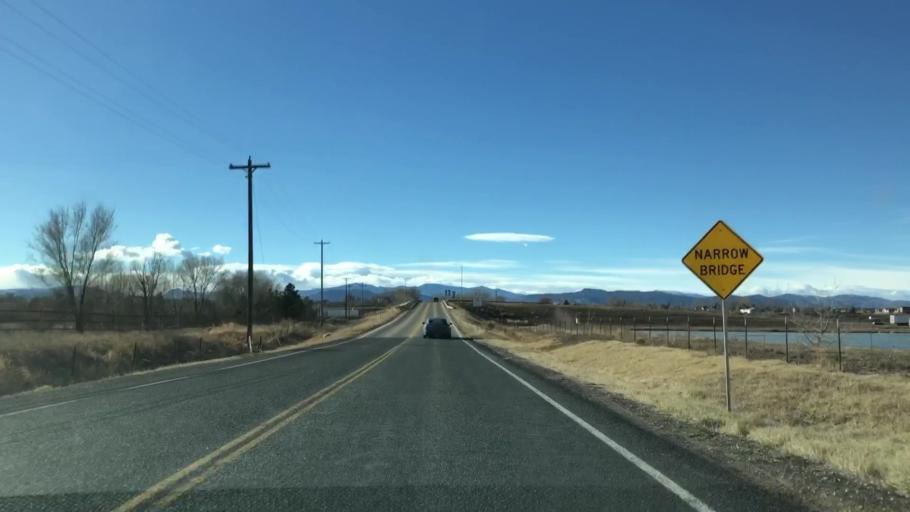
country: US
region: Colorado
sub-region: Weld County
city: Windsor
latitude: 40.5086
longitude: -104.9880
